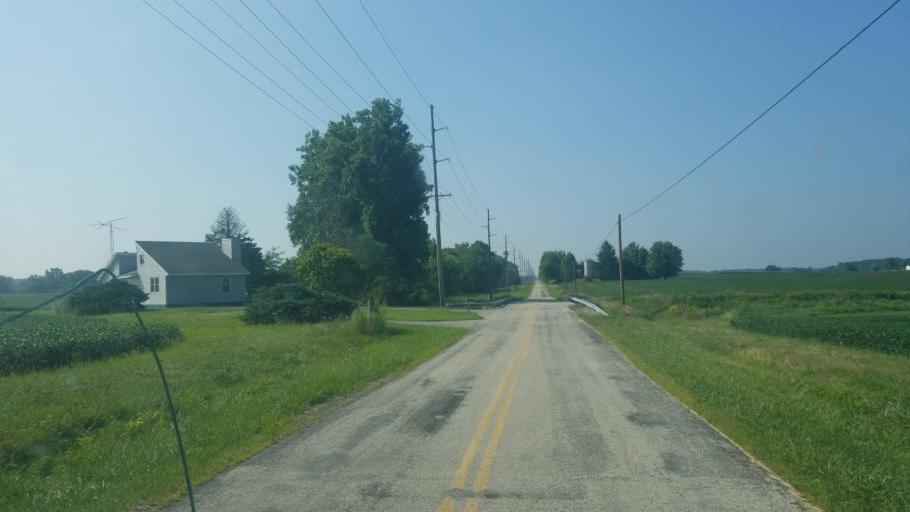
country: US
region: Ohio
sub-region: Wyandot County
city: Upper Sandusky
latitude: 40.6682
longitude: -83.3241
